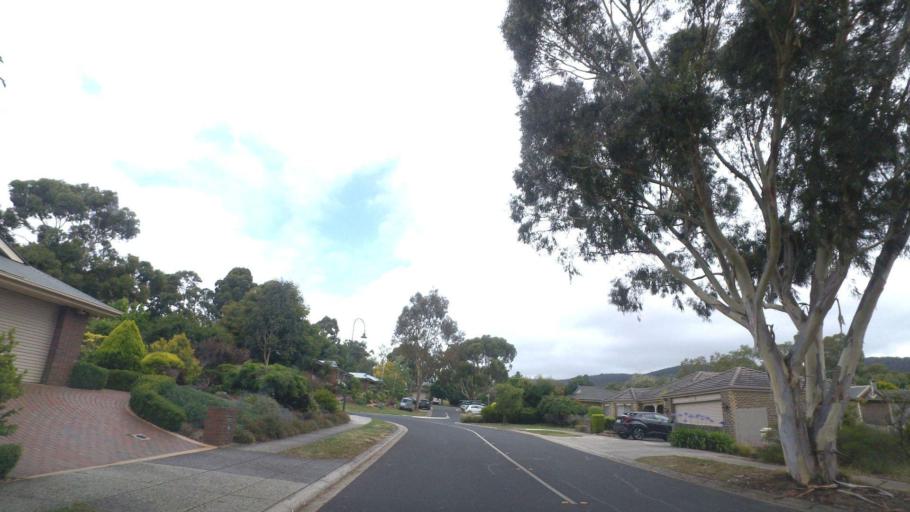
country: AU
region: Victoria
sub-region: Knox
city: The Basin
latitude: -37.8515
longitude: 145.3109
